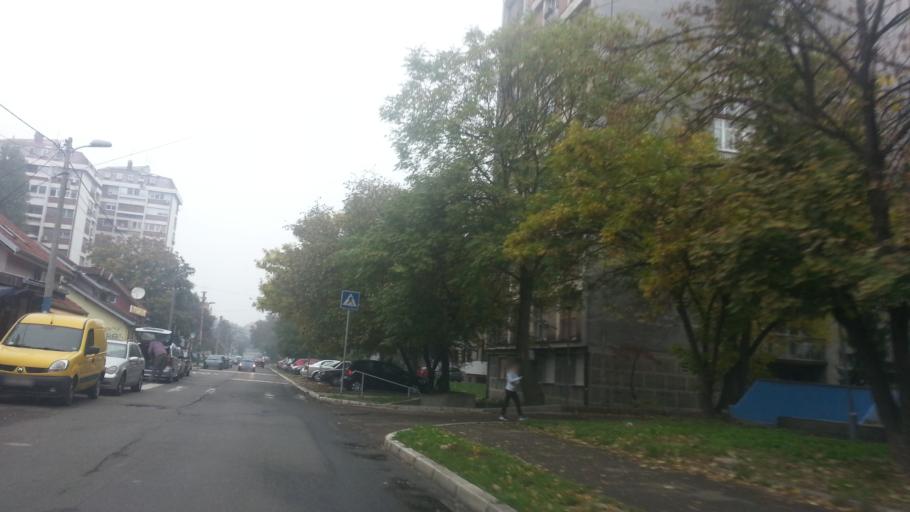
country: RS
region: Central Serbia
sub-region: Belgrade
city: Zemun
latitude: 44.8507
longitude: 20.3865
